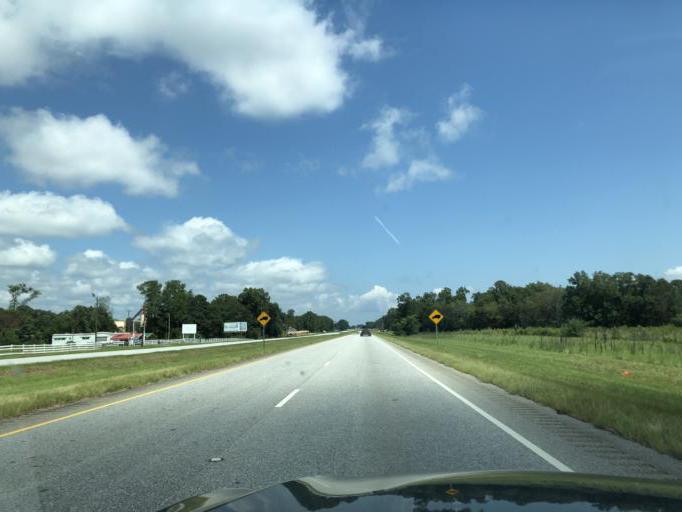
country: US
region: Alabama
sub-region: Barbour County
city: Eufaula
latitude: 31.7909
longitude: -85.1705
